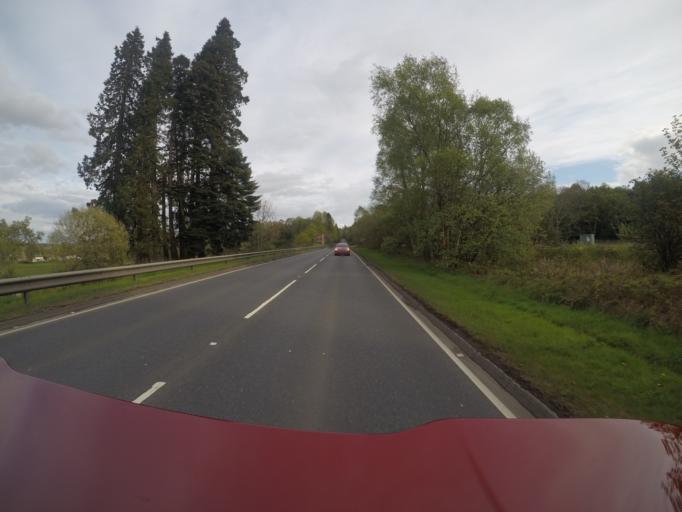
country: GB
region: Scotland
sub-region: West Dunbartonshire
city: Balloch
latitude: 56.0164
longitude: -4.6139
